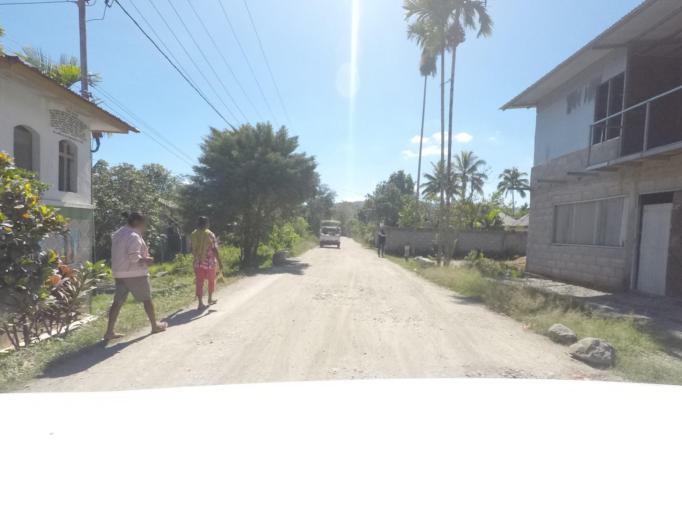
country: TL
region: Ermera
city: Gleno
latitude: -8.7201
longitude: 125.4283
